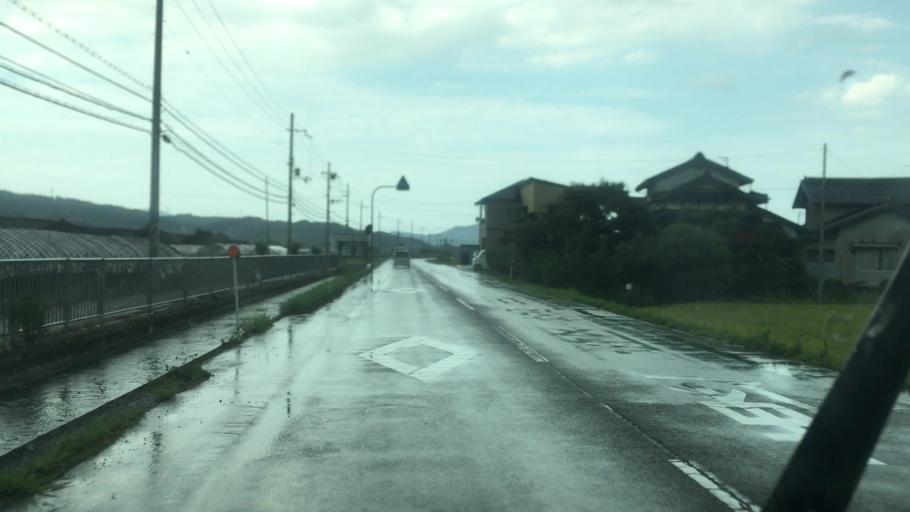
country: JP
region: Hyogo
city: Toyooka
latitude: 35.4923
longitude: 134.8158
